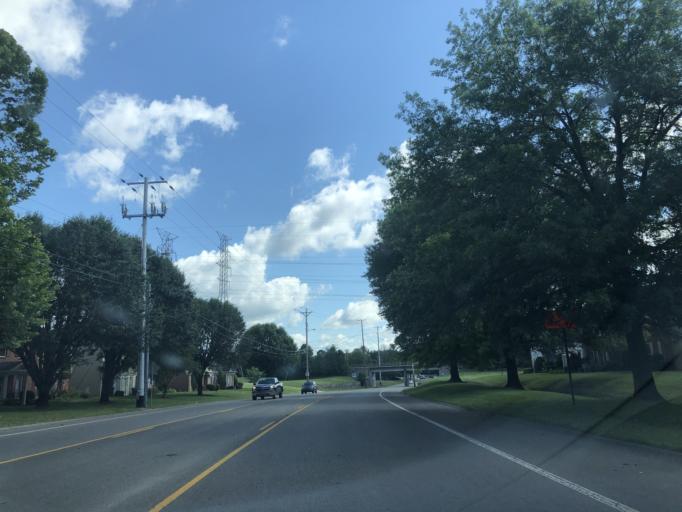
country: US
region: Tennessee
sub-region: Davidson County
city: Belle Meade
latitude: 36.0685
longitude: -86.9492
